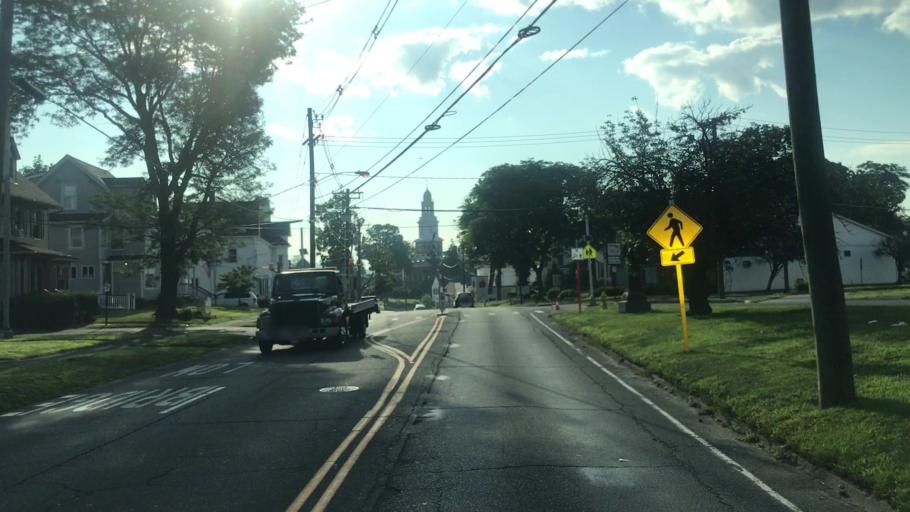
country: US
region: Connecticut
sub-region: Fairfield County
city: Danbury
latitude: 41.3921
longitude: -73.4586
